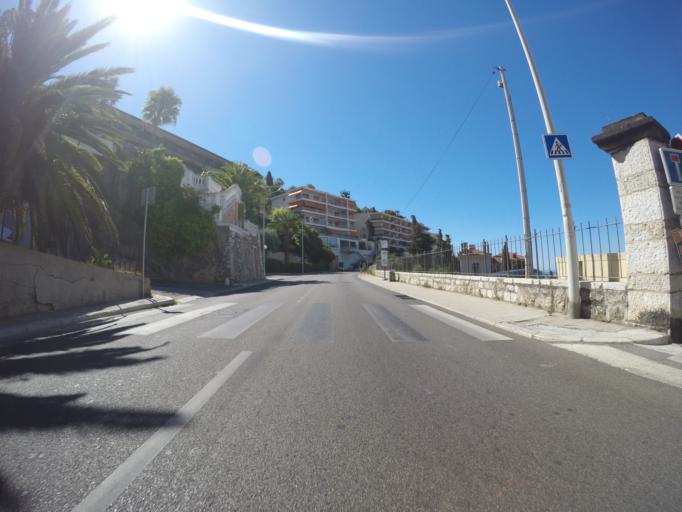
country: FR
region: Provence-Alpes-Cote d'Azur
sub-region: Departement des Alpes-Maritimes
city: Villefranche-sur-Mer
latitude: 43.6951
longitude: 7.2933
